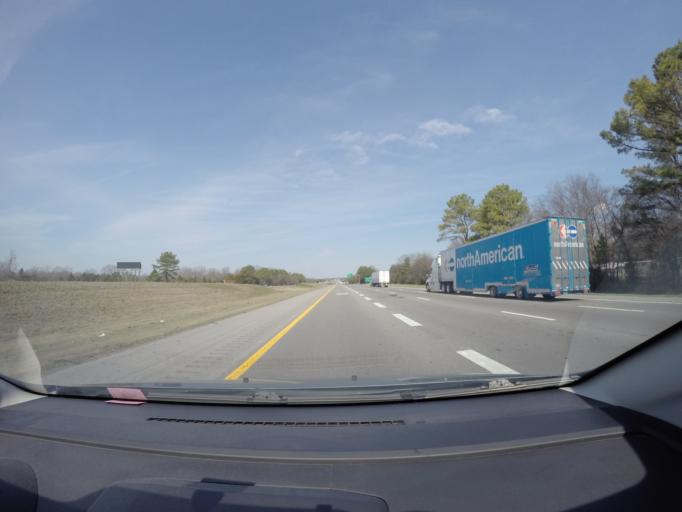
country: US
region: Tennessee
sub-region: Rutherford County
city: Smyrna
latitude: 35.9259
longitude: -86.5219
